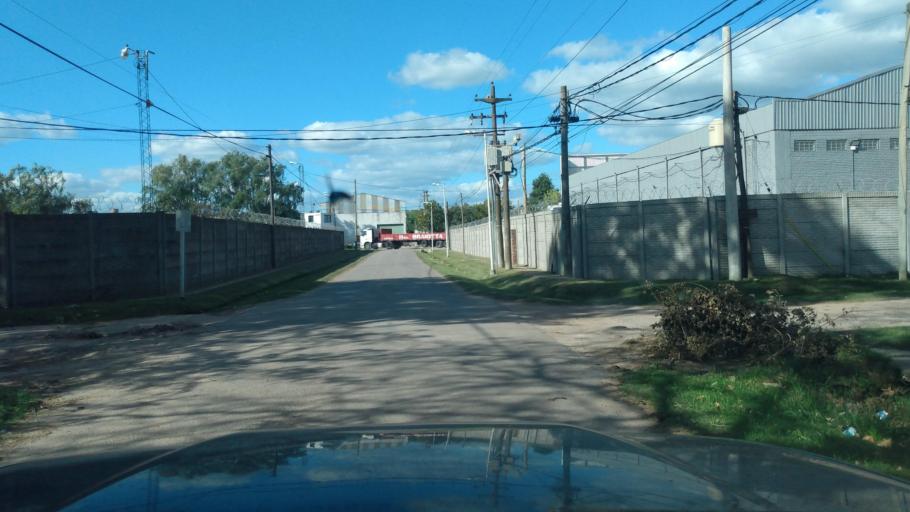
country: AR
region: Buenos Aires
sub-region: Partido de Lujan
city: Lujan
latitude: -34.5817
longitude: -59.0921
